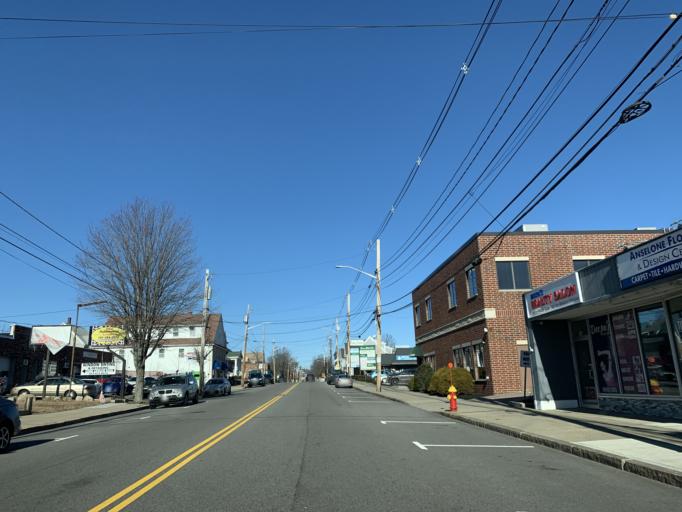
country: US
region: Massachusetts
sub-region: Norfolk County
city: Norwood
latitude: 42.1856
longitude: -71.2031
